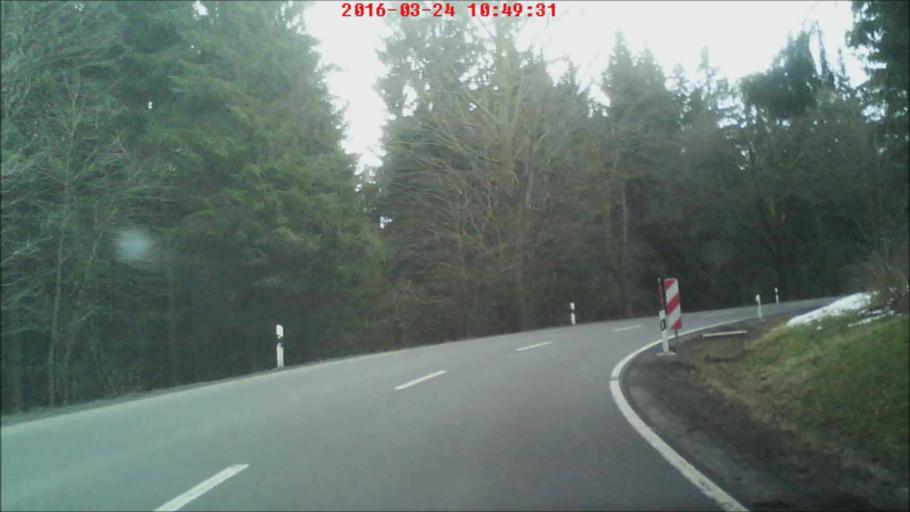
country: DE
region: Thuringia
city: Grossbreitenbach
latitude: 50.5990
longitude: 10.9822
